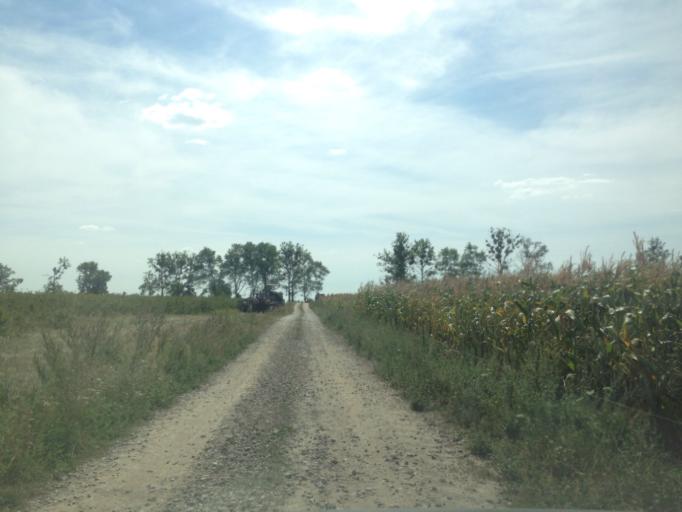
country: PL
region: Kujawsko-Pomorskie
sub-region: Powiat brodnicki
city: Gorzno
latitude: 53.2116
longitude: 19.6265
